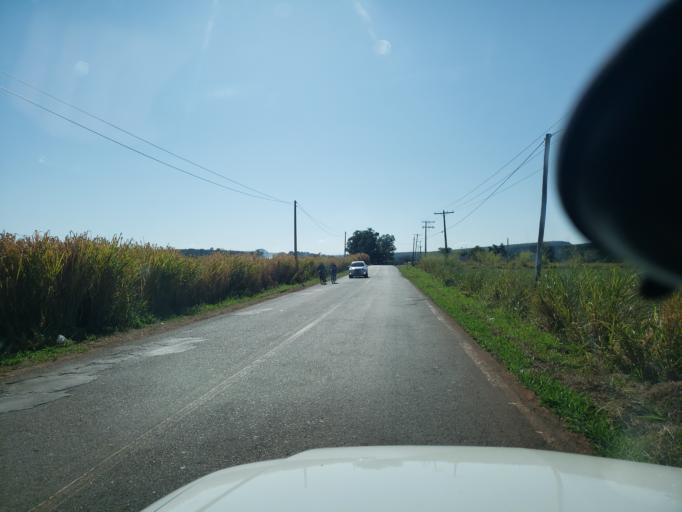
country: BR
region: Sao Paulo
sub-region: Moji-Guacu
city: Mogi-Gaucu
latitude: -22.3379
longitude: -46.8848
